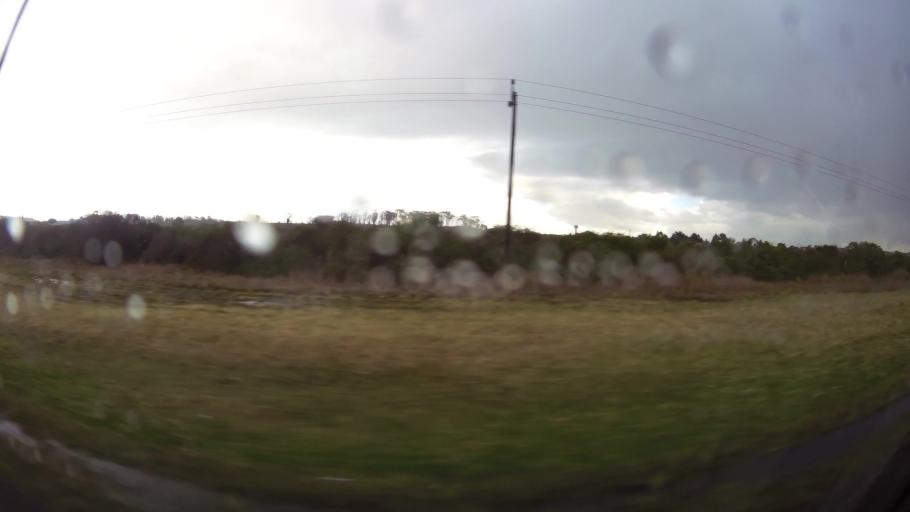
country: ZA
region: Western Cape
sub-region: Eden District Municipality
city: Mossel Bay
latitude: -34.1829
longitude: 22.0947
